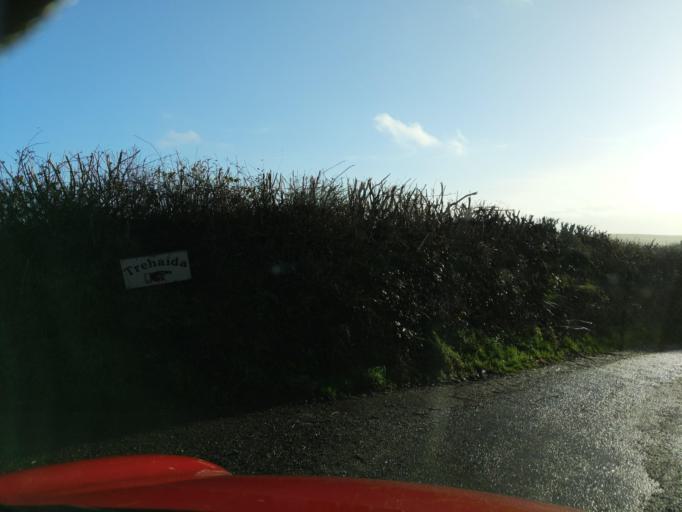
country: GB
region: England
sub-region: Cornwall
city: Fowey
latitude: 50.3516
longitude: -4.6062
